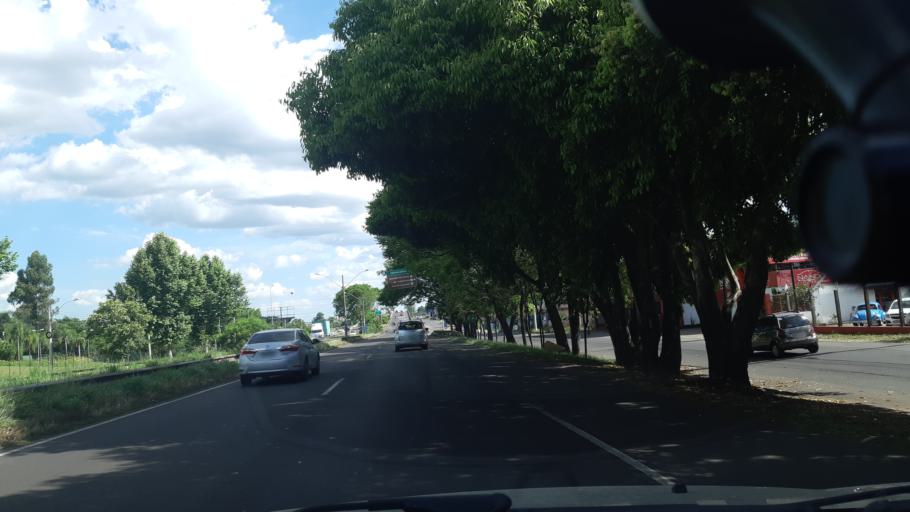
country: BR
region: Rio Grande do Sul
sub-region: Novo Hamburgo
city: Novo Hamburgo
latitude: -29.6643
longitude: -51.1437
